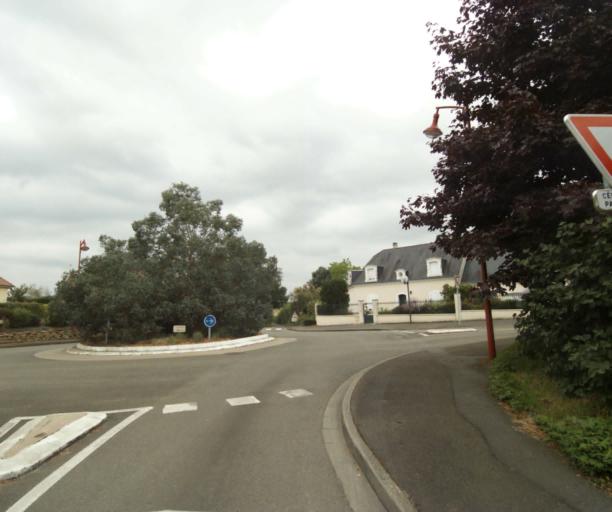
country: FR
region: Pays de la Loire
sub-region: Departement de la Sarthe
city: Solesmes
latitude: 47.8512
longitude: -0.2914
